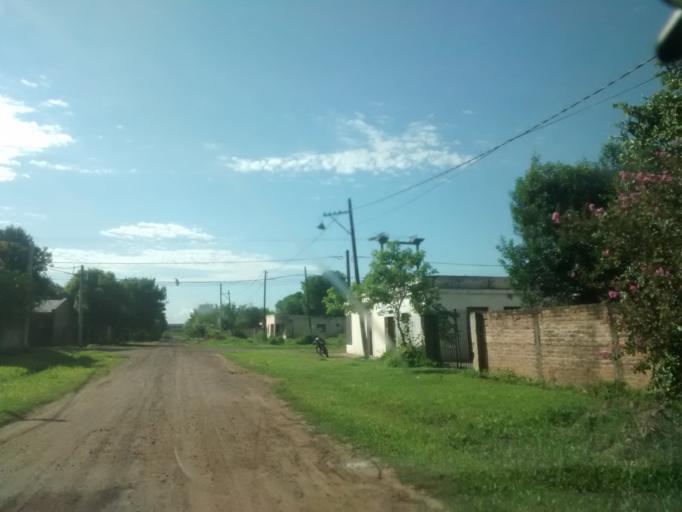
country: AR
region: Chaco
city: Puerto Tirol
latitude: -27.3758
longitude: -59.0961
